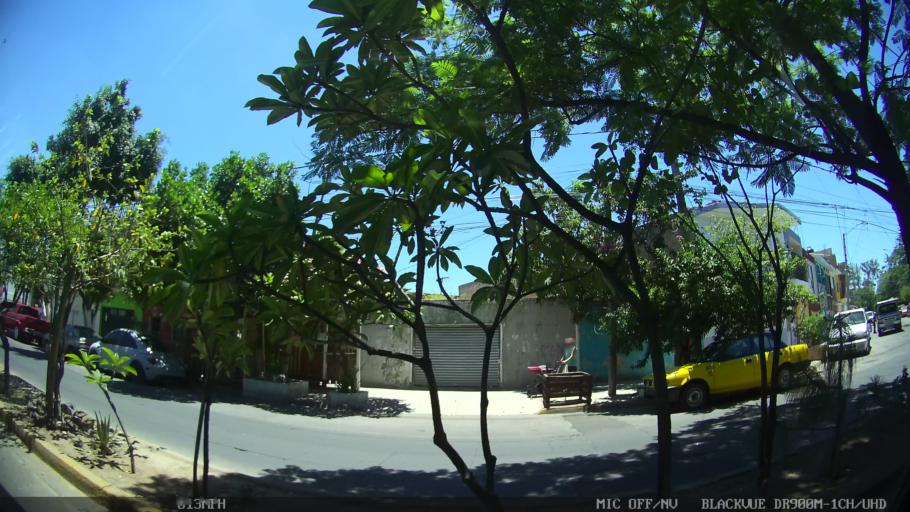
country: MX
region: Jalisco
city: Tlaquepaque
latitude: 20.6674
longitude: -103.2806
